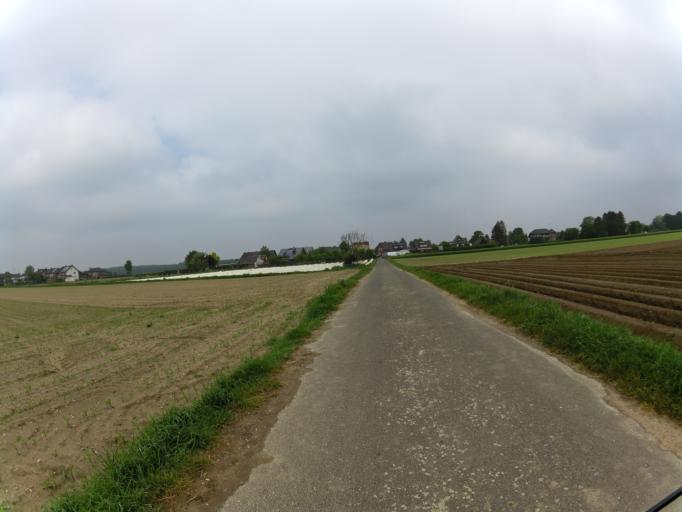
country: DE
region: North Rhine-Westphalia
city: Geilenkirchen
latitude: 50.9837
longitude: 6.0846
